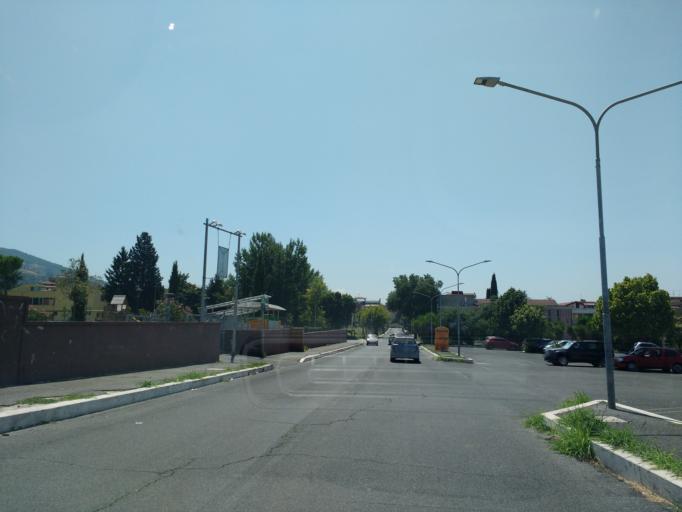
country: IT
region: Latium
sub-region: Citta metropolitana di Roma Capitale
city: Villa Adriana
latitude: 41.9543
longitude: 12.7710
